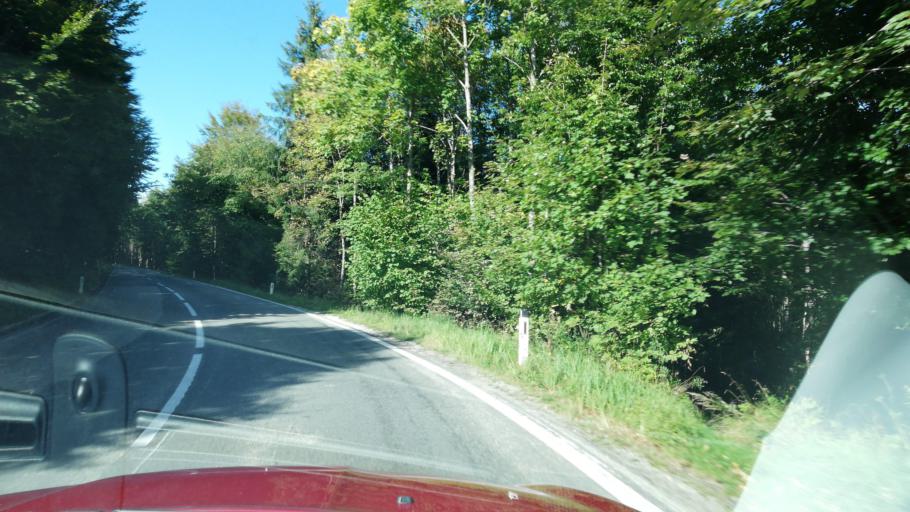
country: AT
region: Upper Austria
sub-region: Politischer Bezirk Vocklabruck
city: Redleiten
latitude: 48.1112
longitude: 13.5660
